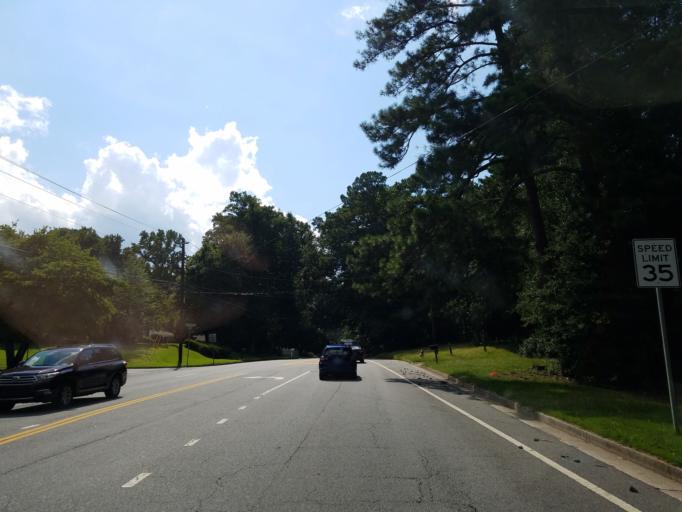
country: US
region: Georgia
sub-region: Fulton County
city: Sandy Springs
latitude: 33.9191
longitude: -84.3655
